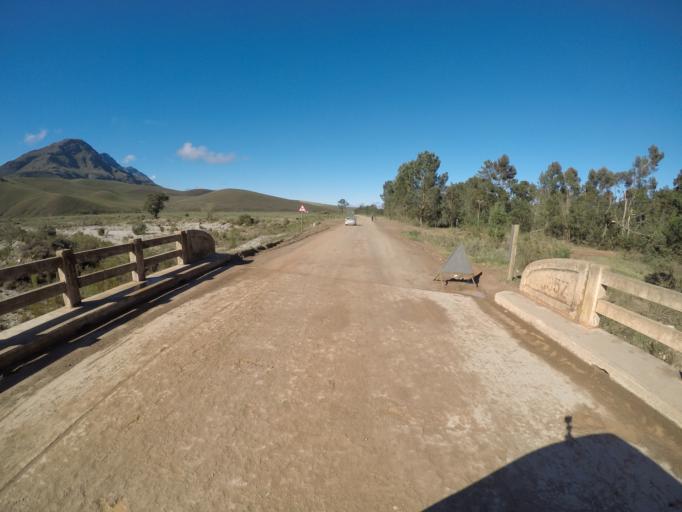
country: ZA
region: Western Cape
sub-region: Overberg District Municipality
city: Caledon
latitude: -34.0533
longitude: 19.6142
